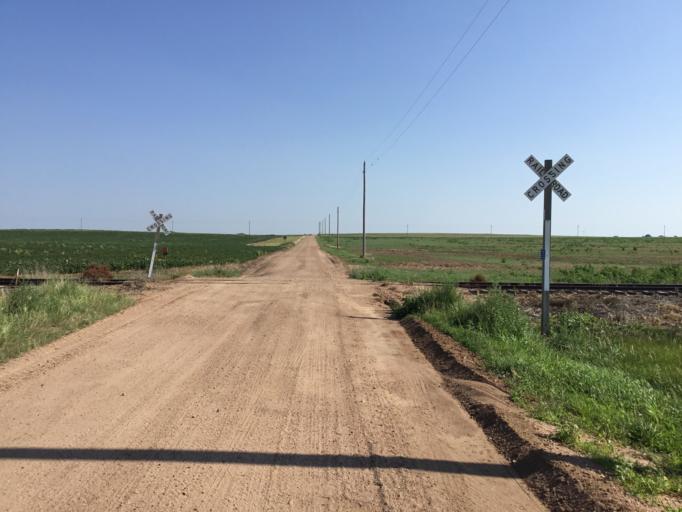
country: US
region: Kansas
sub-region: Pratt County
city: Pratt
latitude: 37.5097
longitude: -98.7574
